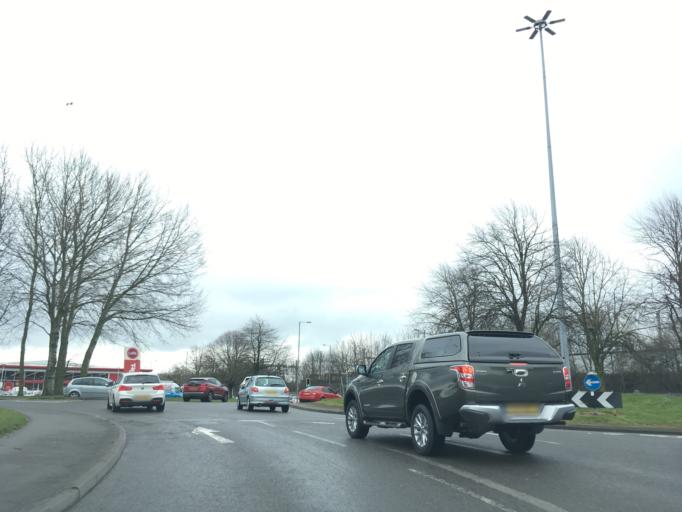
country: GB
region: England
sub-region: Borough of Swindon
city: Swindon
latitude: 51.5681
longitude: -1.7833
